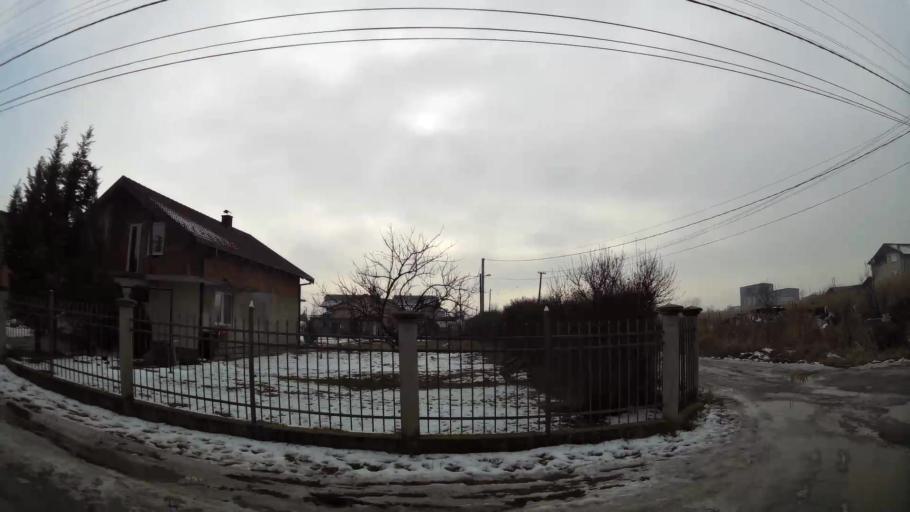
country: MK
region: Ilinden
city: Ilinden
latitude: 41.9900
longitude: 21.5781
